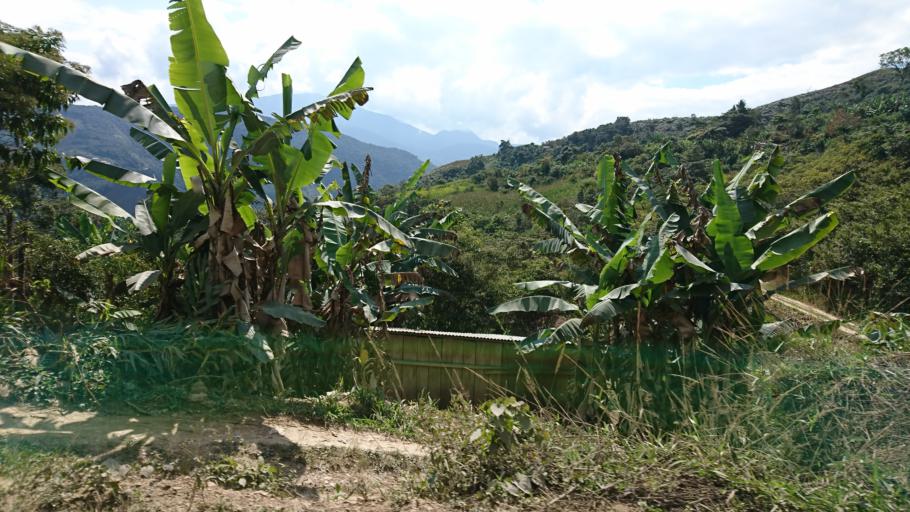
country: BO
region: La Paz
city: Coroico
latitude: -16.1291
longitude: -67.7517
